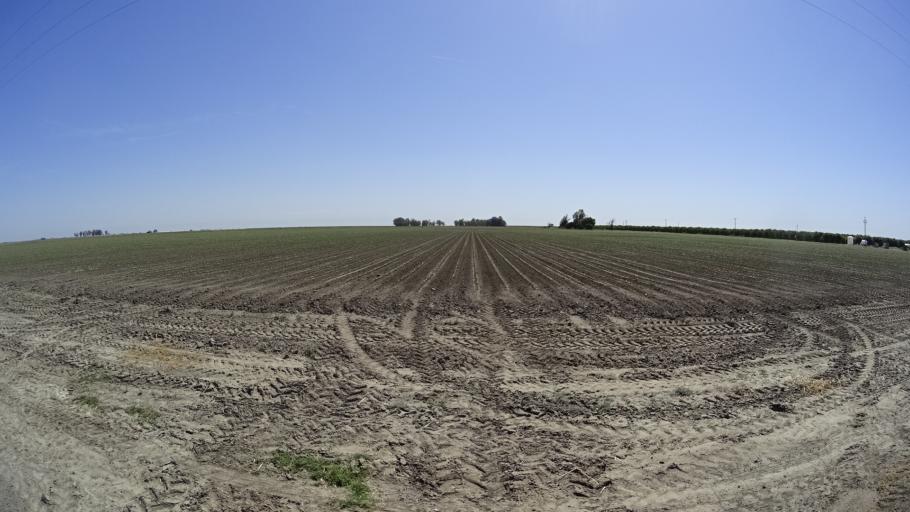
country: US
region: California
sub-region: Kings County
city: Stratford
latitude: 36.1686
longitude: -119.7802
